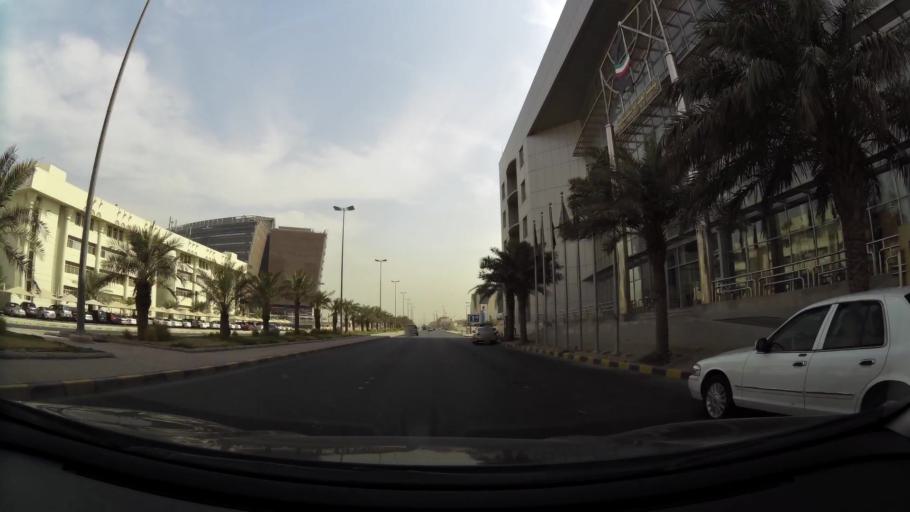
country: KW
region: Al Farwaniyah
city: Janub as Surrah
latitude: 29.2721
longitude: 48.0174
